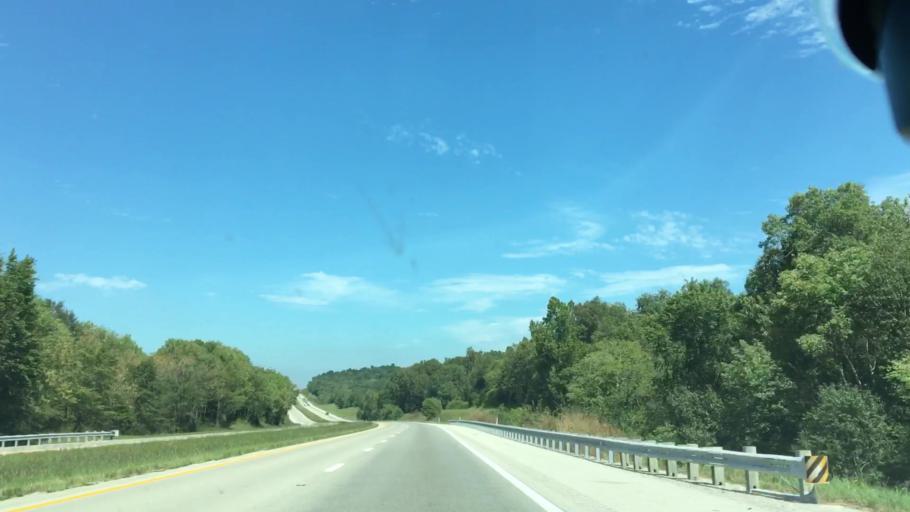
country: US
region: Kentucky
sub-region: Christian County
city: Hopkinsville
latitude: 36.9287
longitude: -87.4707
